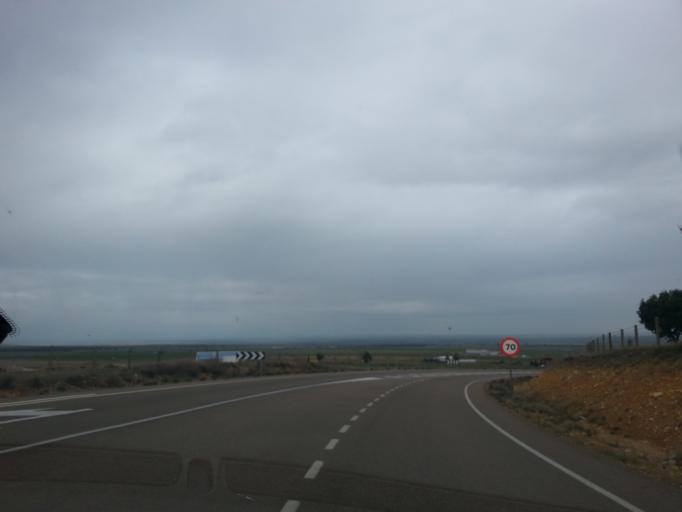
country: ES
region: Castille and Leon
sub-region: Provincia de Salamanca
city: Tamames
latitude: 40.6573
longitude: -6.1183
